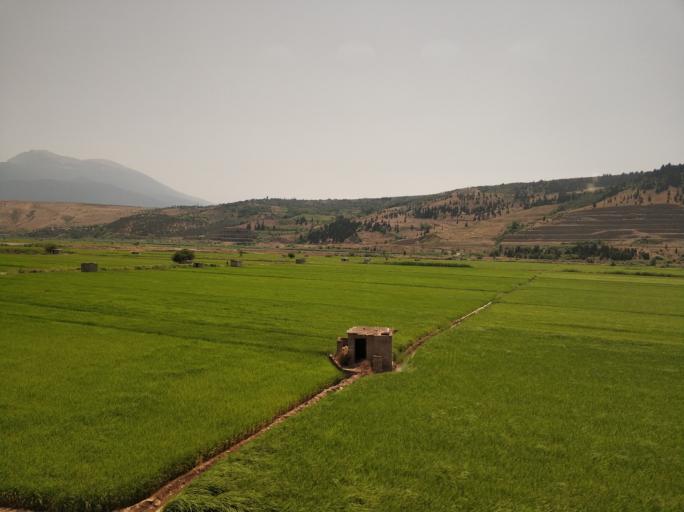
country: IR
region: Gilan
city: Pa'in-e Bazar-e Rudbar
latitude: 36.8707
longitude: 49.4917
